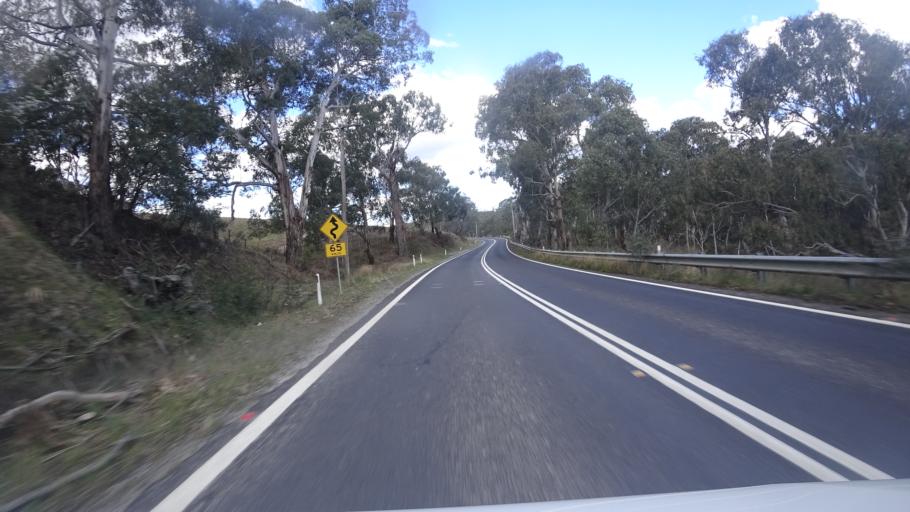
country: AU
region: New South Wales
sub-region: Lithgow
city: Bowenfels
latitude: -33.5483
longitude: 150.1552
